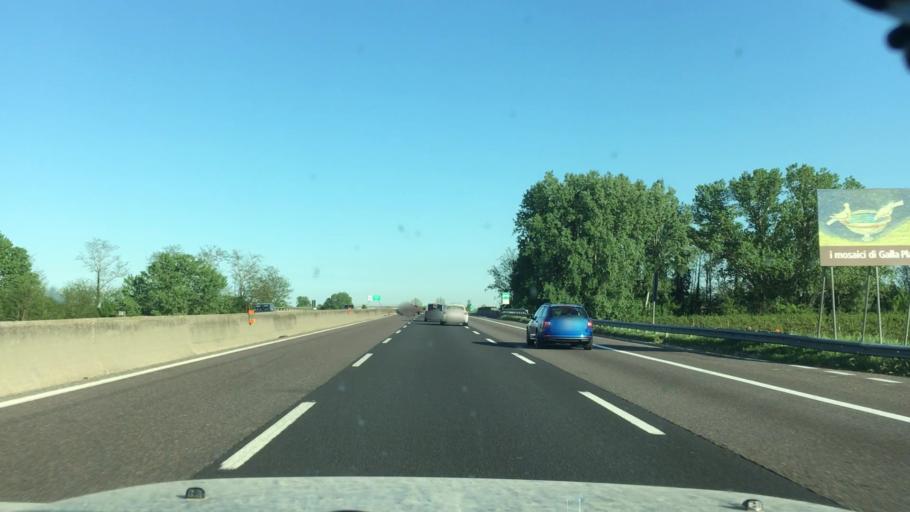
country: IT
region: Emilia-Romagna
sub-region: Provincia di Bologna
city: Mordano
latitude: 44.3646
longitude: 11.7842
